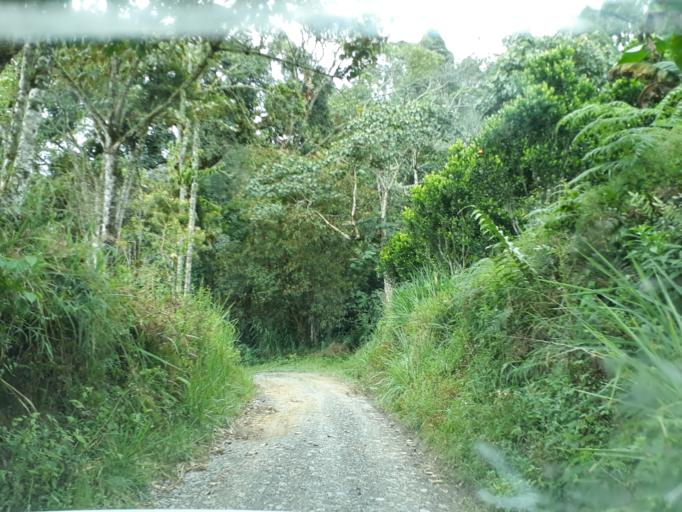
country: CO
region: Cundinamarca
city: Pacho
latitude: 5.1617
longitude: -74.2363
